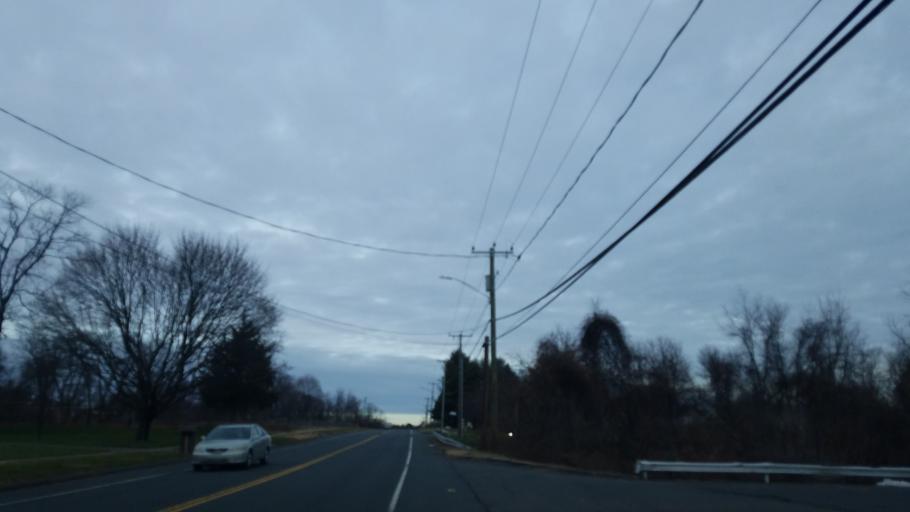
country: US
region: Connecticut
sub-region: Hartford County
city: Newington
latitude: 41.7114
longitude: -72.7458
